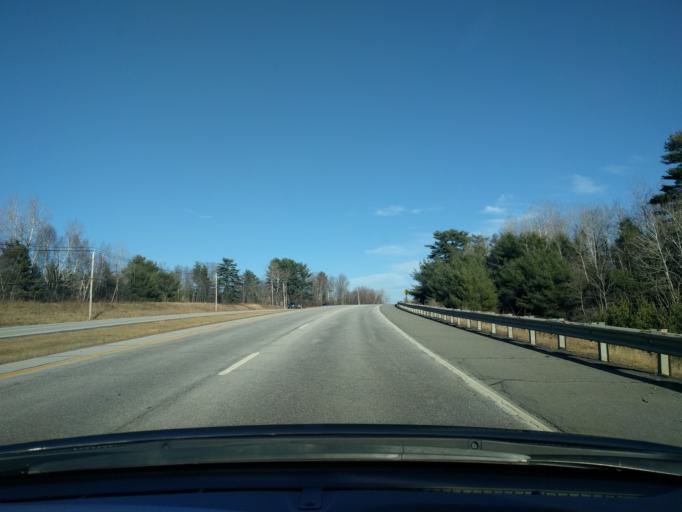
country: US
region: Maine
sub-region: Penobscot County
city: Hampden
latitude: 44.7513
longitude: -68.8438
